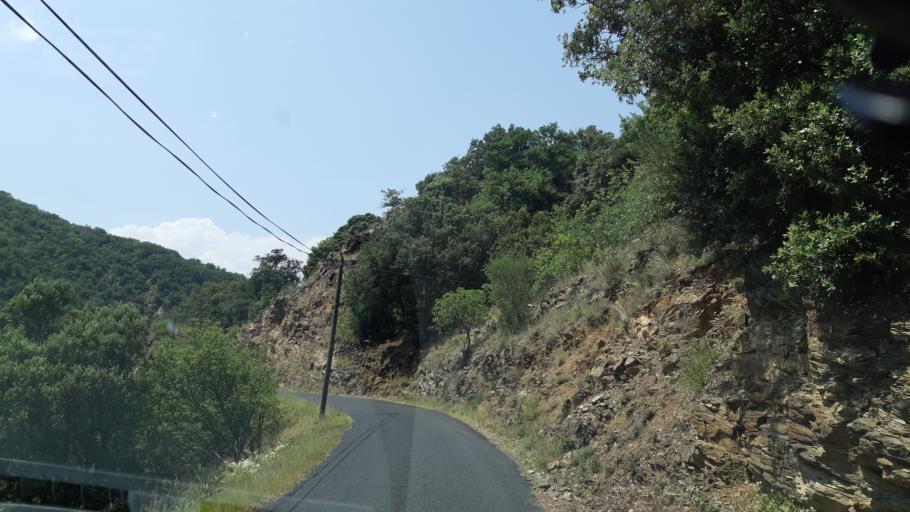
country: FR
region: Languedoc-Roussillon
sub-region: Departement des Pyrenees-Orientales
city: Vinca
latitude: 42.6077
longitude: 2.5121
